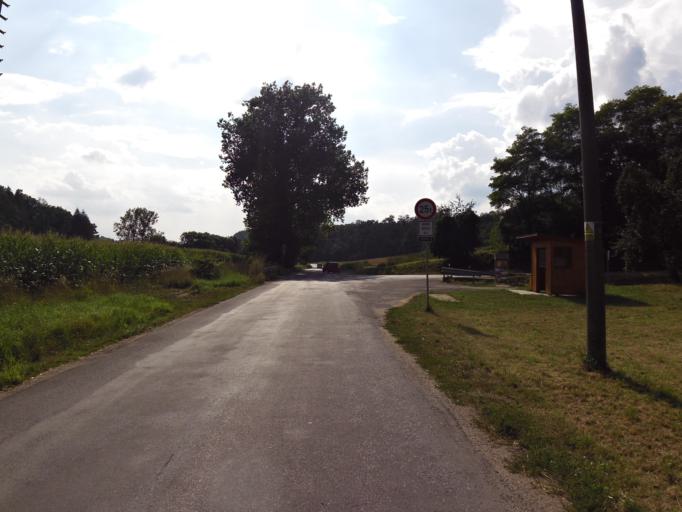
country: CZ
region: Central Bohemia
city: Mnichovo Hradiste
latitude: 50.5695
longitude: 15.0016
